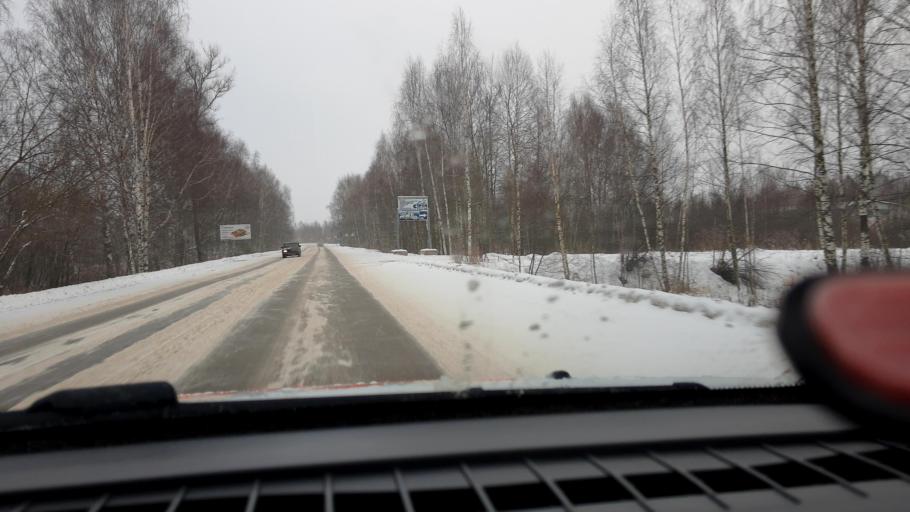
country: RU
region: Nizjnij Novgorod
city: Afonino
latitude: 56.3150
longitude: 44.2180
